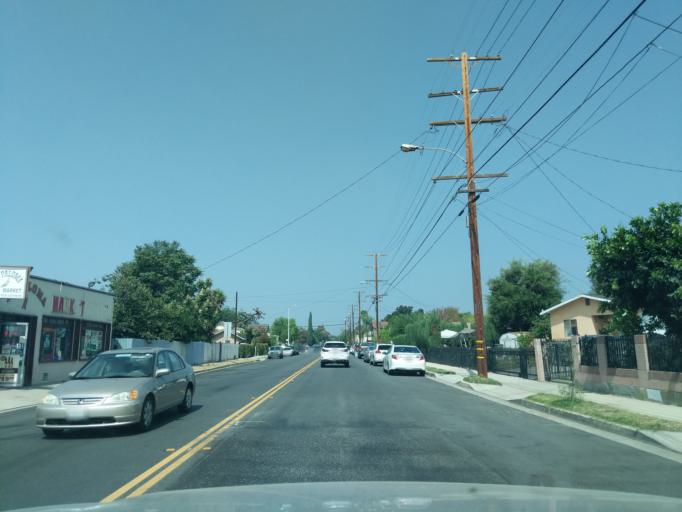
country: US
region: California
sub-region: Los Angeles County
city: East San Gabriel
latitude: 34.0921
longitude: -118.0938
